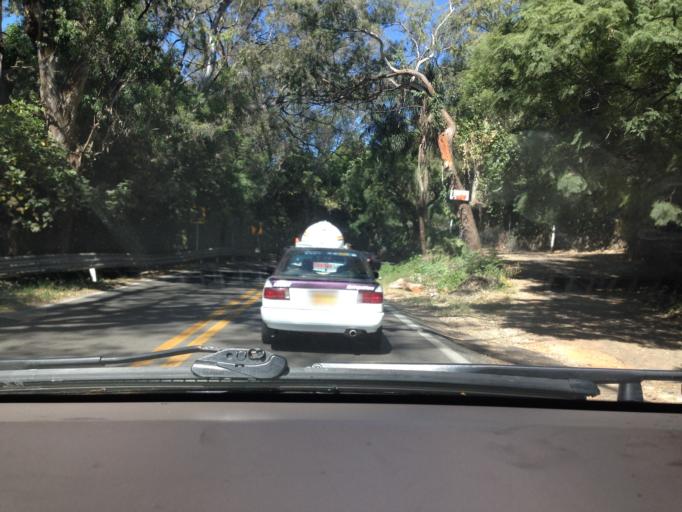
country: MX
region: Morelos
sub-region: Cuernavaca
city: Fraccionamiento Lomas de Ahuatlan
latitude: 18.9741
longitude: -99.2519
